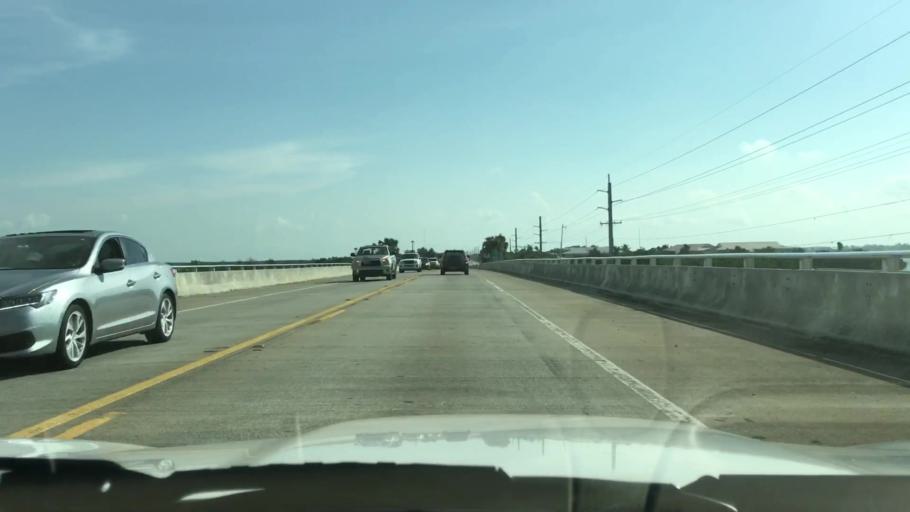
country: US
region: Florida
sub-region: Monroe County
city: Cudjoe Key
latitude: 24.6627
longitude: -81.4654
